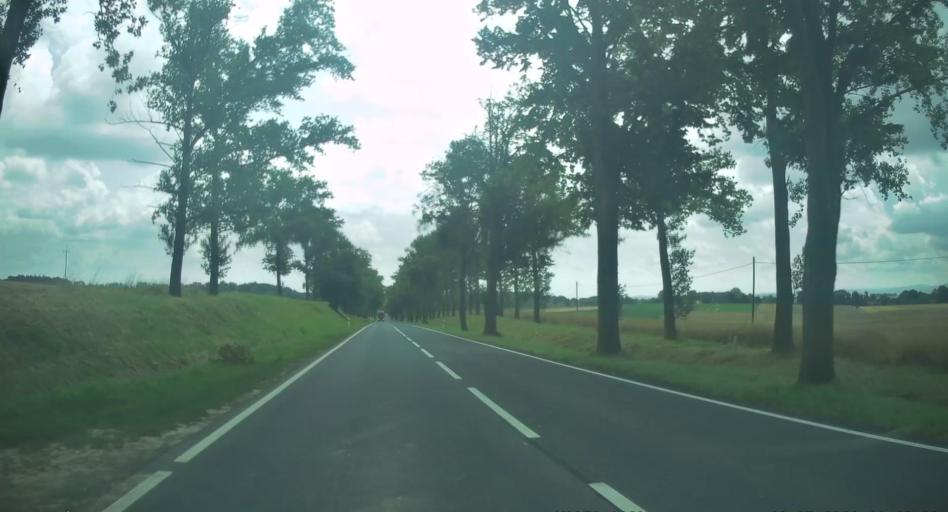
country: PL
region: Opole Voivodeship
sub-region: Powiat prudnicki
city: Laka Prudnicka
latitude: 50.3895
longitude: 17.5176
